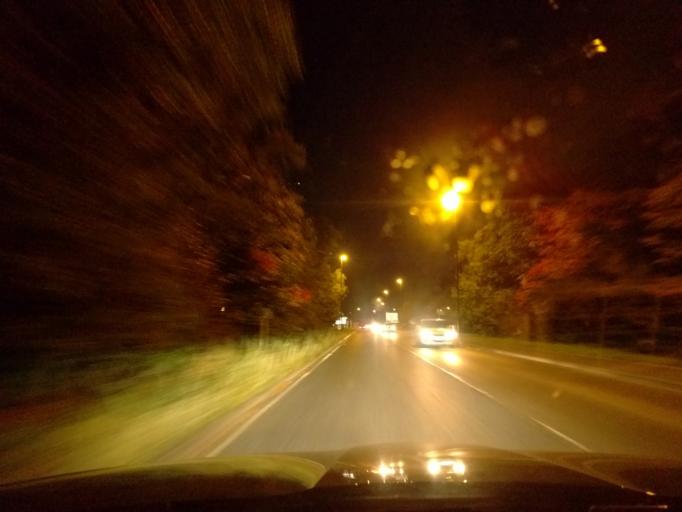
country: GB
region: England
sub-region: Borough of North Tyneside
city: Wallsend
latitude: 55.0170
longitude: -1.5452
